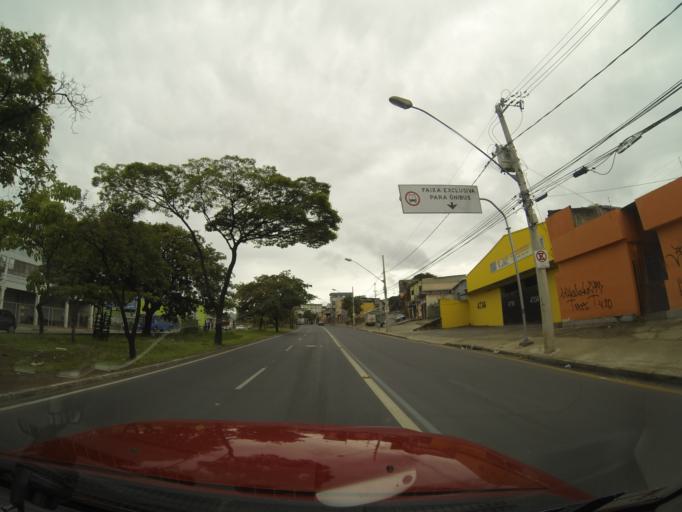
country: BR
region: Minas Gerais
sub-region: Belo Horizonte
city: Belo Horizonte
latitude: -19.9078
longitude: -43.9834
